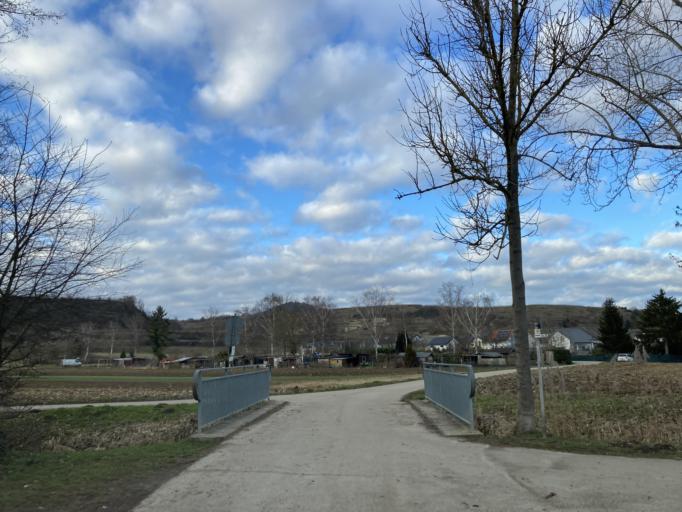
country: DE
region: Baden-Wuerttemberg
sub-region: Freiburg Region
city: Botzingen
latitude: 48.0629
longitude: 7.7102
